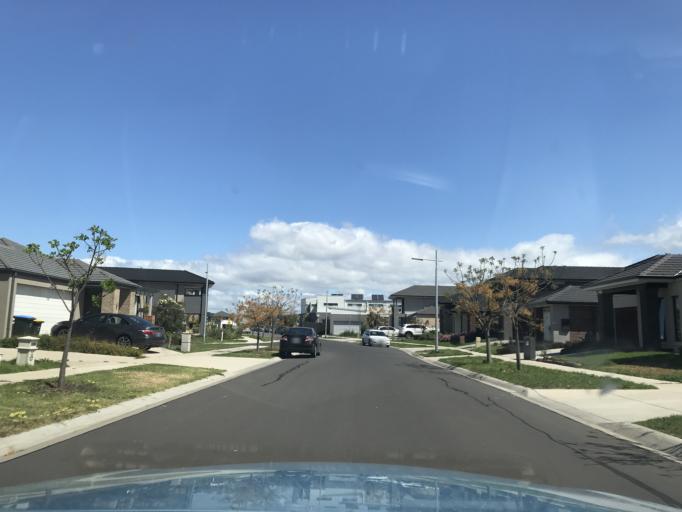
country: AU
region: Victoria
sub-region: Wyndham
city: Williams Landing
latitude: -37.8639
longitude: 144.7375
